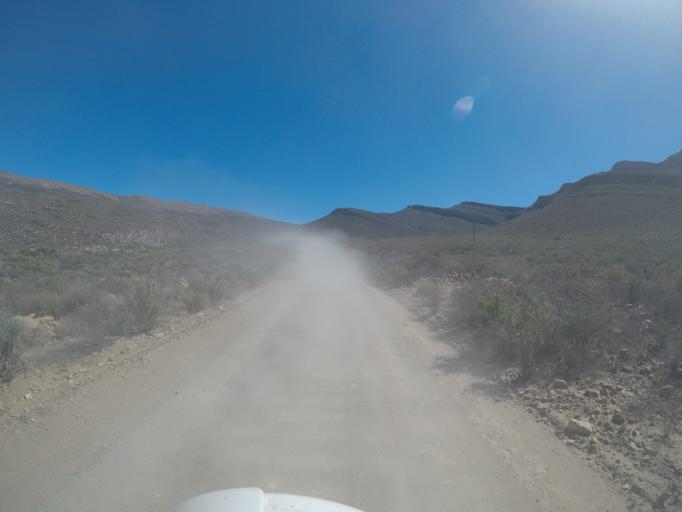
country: ZA
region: Western Cape
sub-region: West Coast District Municipality
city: Clanwilliam
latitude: -32.6283
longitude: 19.3924
